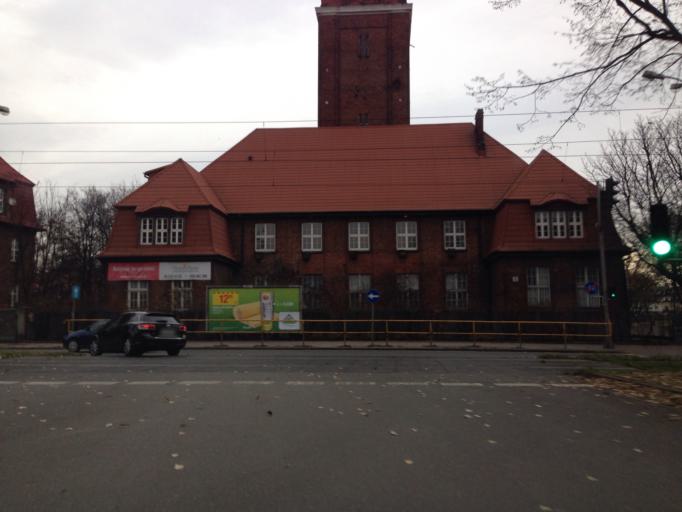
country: PL
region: Pomeranian Voivodeship
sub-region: Gdansk
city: Gdansk
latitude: 54.3852
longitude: 18.6121
